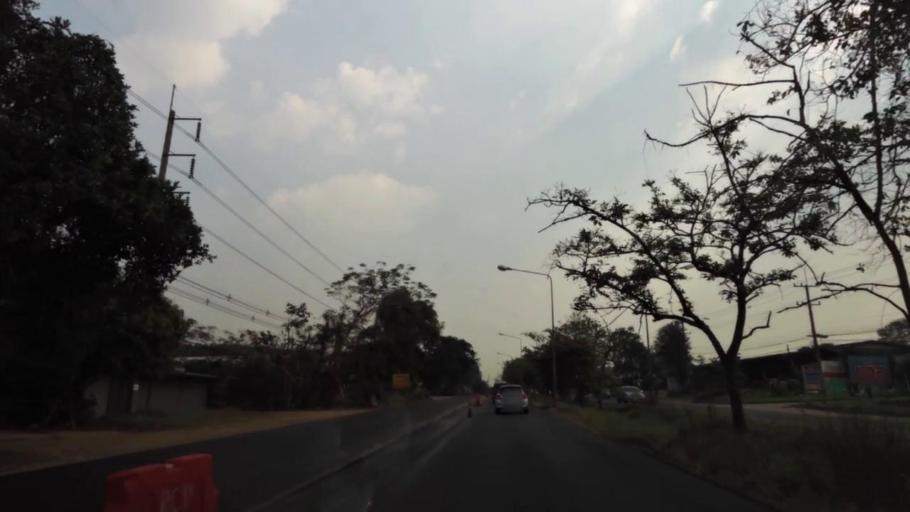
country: TH
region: Rayong
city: Klaeng
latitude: 12.8358
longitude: 101.6257
